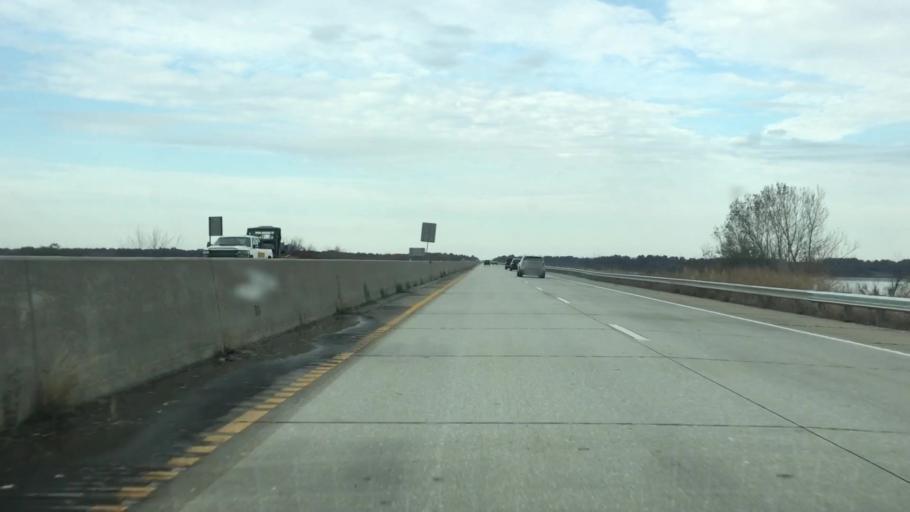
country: US
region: Missouri
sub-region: Henry County
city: Clinton
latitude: 38.2696
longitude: -93.7601
